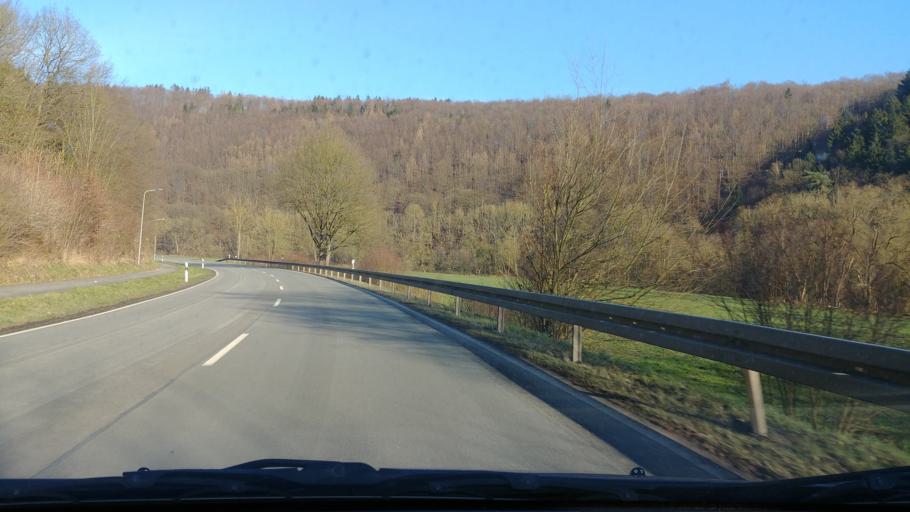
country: DE
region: Lower Saxony
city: Bad Karlshafen
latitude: 51.6318
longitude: 9.4676
